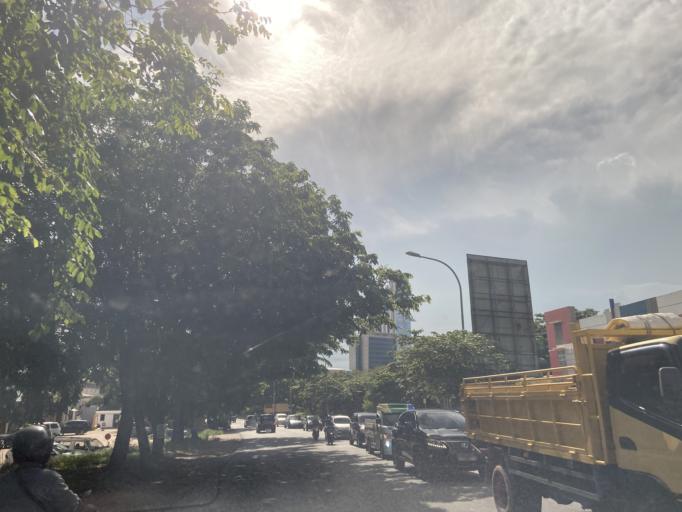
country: SG
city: Singapore
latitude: 1.1157
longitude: 104.0504
